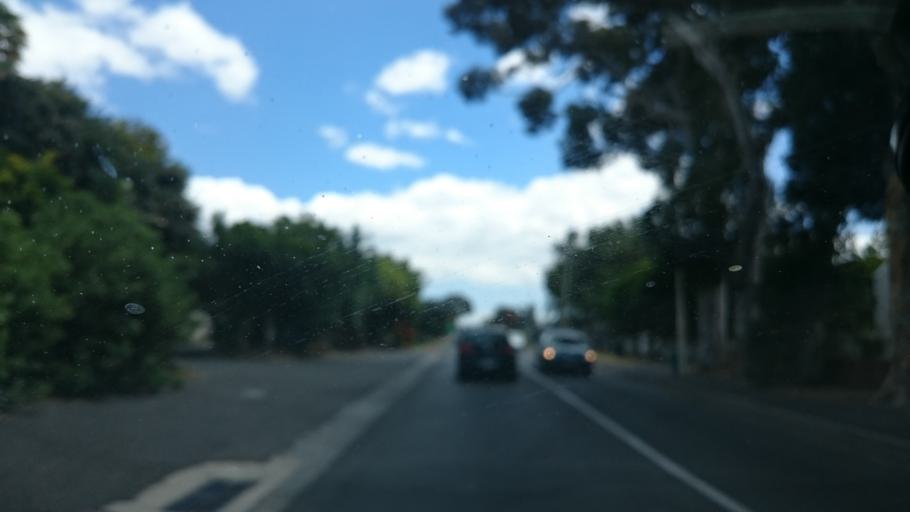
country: ZA
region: Western Cape
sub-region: City of Cape Town
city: Bergvliet
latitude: -34.0442
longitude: 18.4633
